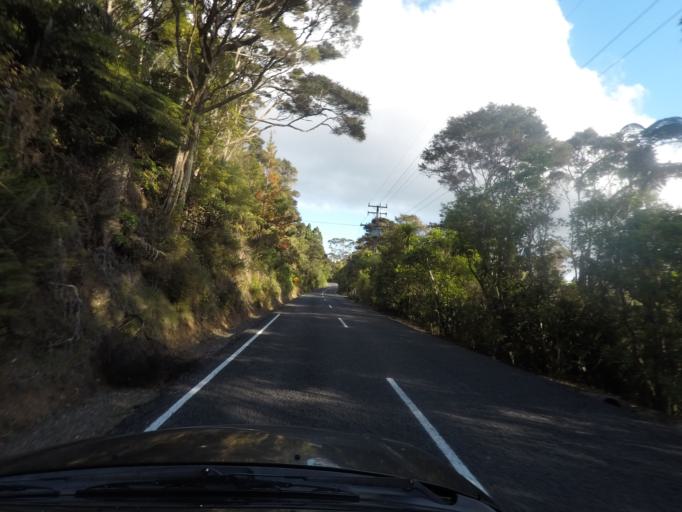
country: NZ
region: Auckland
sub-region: Auckland
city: Titirangi
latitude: -36.9370
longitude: 174.6183
